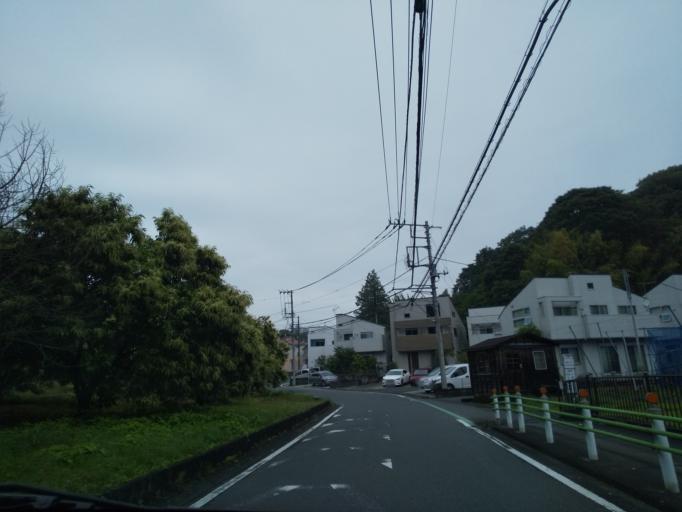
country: JP
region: Tokyo
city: Hino
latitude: 35.6484
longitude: 139.4272
